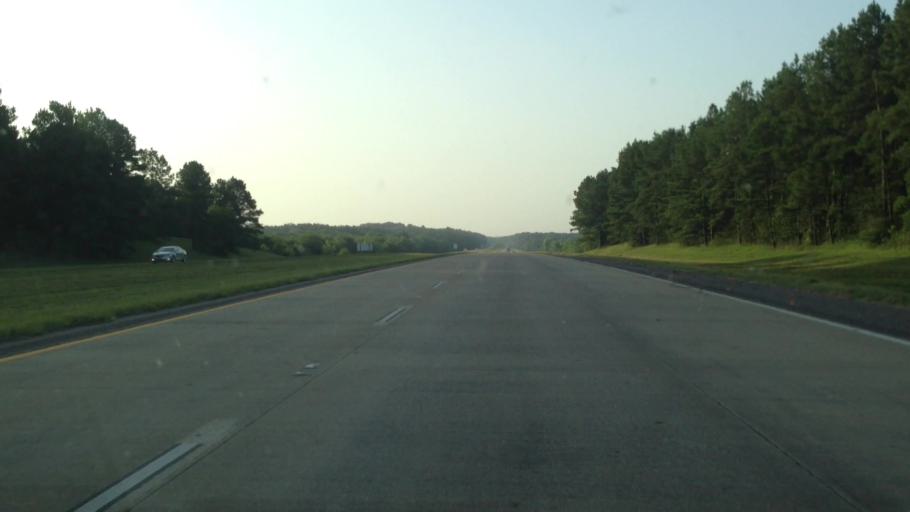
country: US
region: Louisiana
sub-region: Grant Parish
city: Colfax
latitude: 31.4900
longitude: -92.8558
